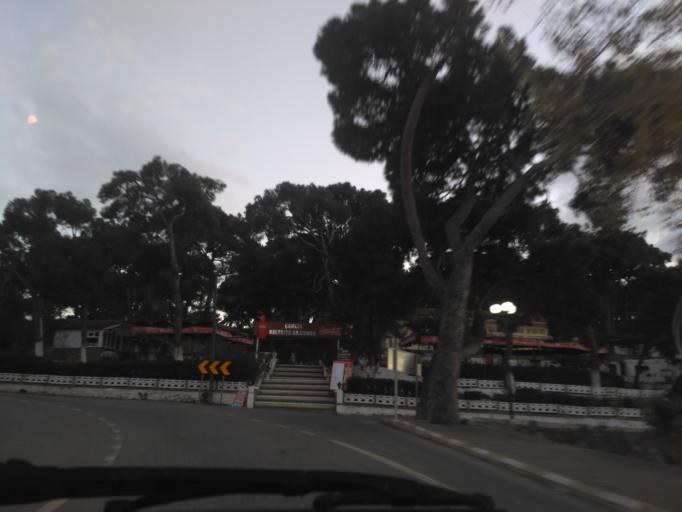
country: TR
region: Balikesir
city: Ayvalik
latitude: 39.3002
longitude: 26.6640
